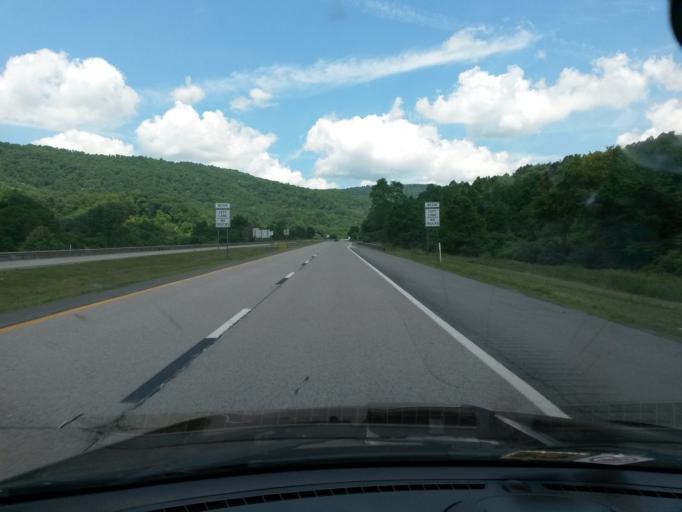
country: US
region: West Virginia
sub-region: Summers County
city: Hinton
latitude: 37.8135
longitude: -80.8140
